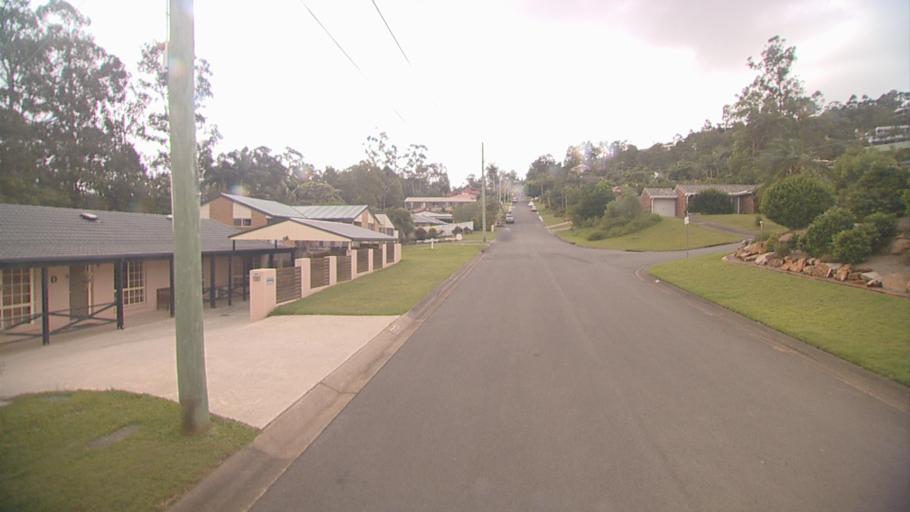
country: AU
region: Queensland
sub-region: Logan
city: Slacks Creek
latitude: -27.6623
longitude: 153.1904
